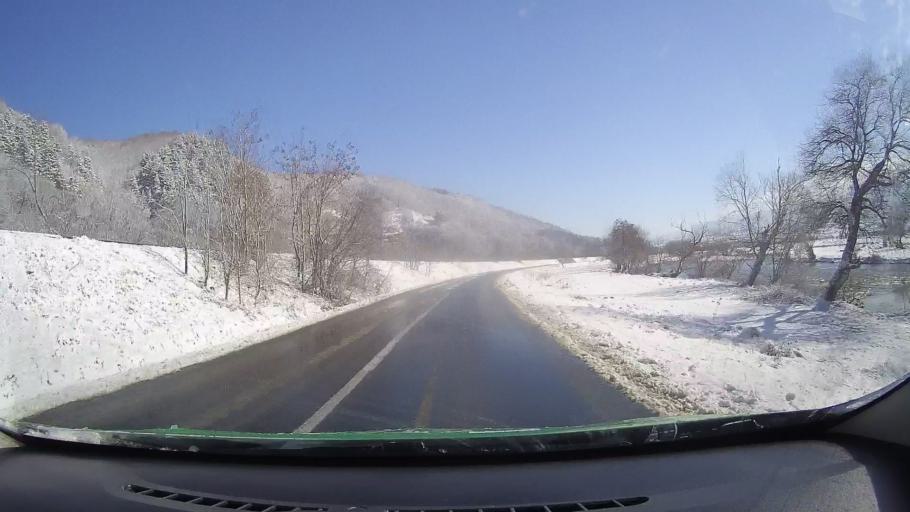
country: RO
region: Sibiu
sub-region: Comuna Talmaciu
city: Talmaciu
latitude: 45.6614
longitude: 24.2810
